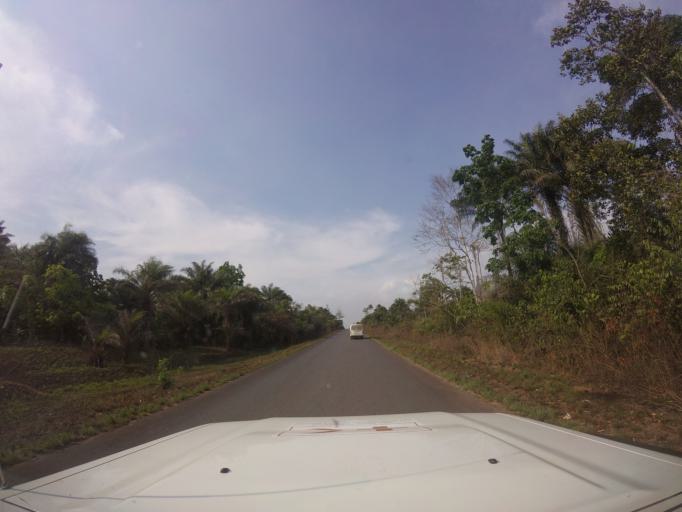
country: LR
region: Bomi
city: Tubmanburg
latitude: 6.7465
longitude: -10.8547
